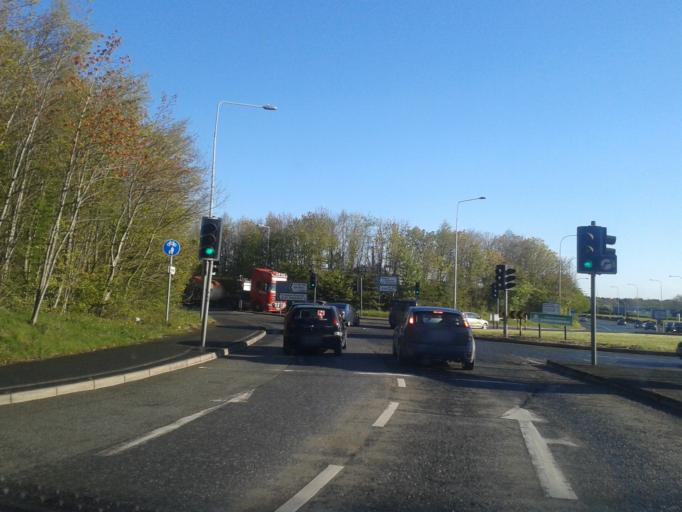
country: IE
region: Leinster
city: Kinsealy-Drinan
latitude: 53.4338
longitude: -6.2291
